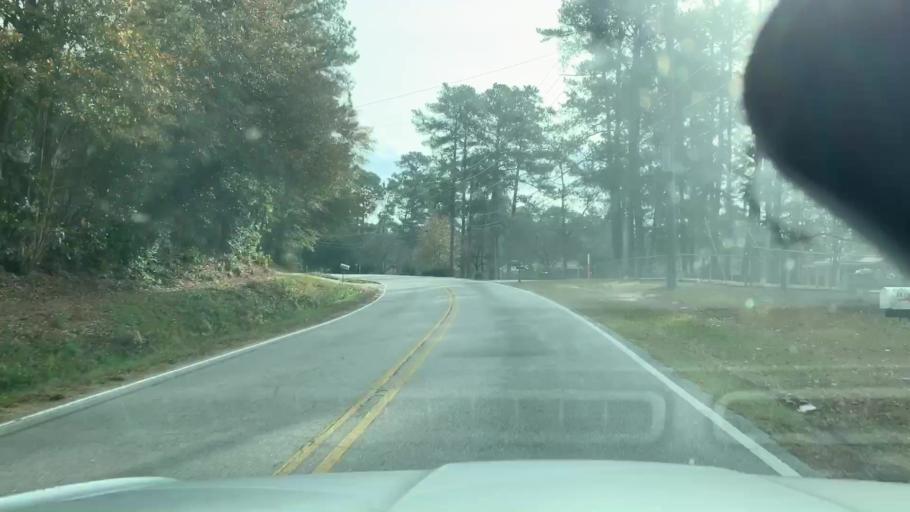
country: US
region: South Carolina
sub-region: Richland County
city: Woodfield
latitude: 34.0822
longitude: -80.9311
